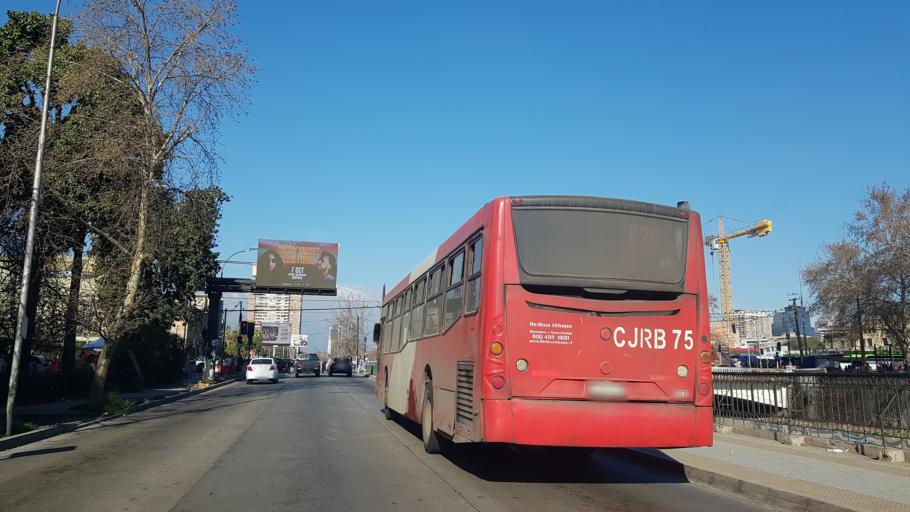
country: CL
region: Santiago Metropolitan
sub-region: Provincia de Santiago
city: Santiago
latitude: -33.4314
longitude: -70.6538
